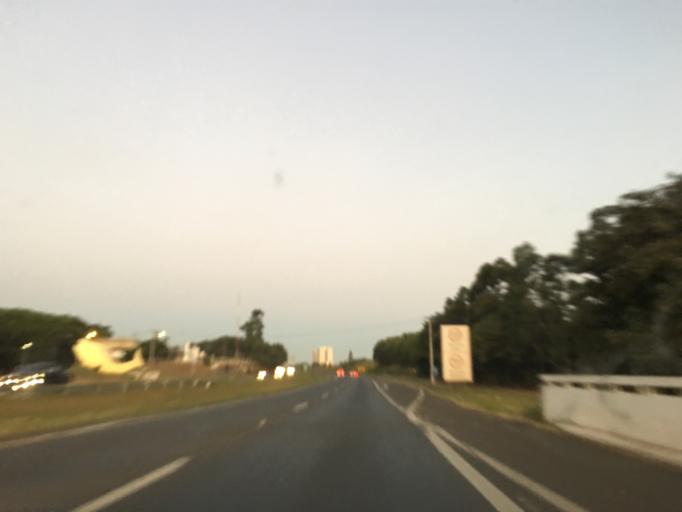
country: BR
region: Sao Paulo
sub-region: Piracicaba
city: Piracicaba
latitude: -22.7179
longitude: -47.6234
